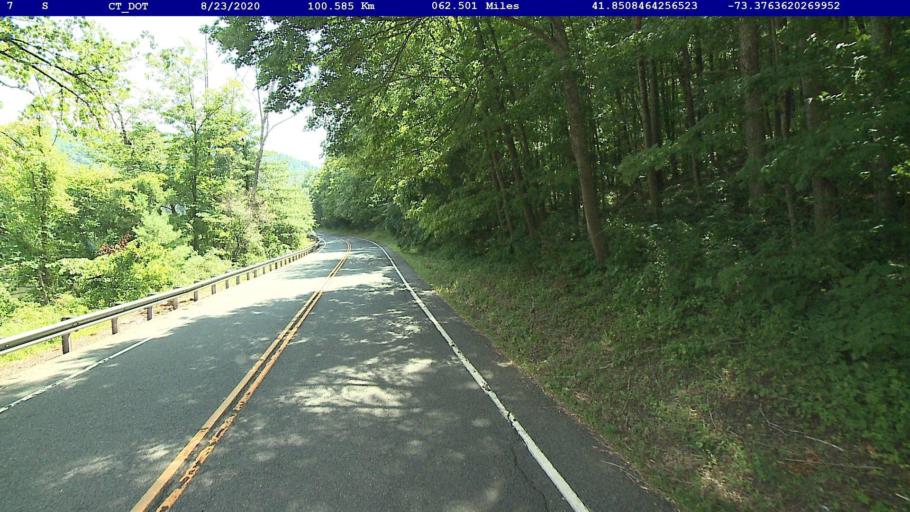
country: US
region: Connecticut
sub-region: Litchfield County
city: Kent
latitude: 41.8508
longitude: -73.3764
